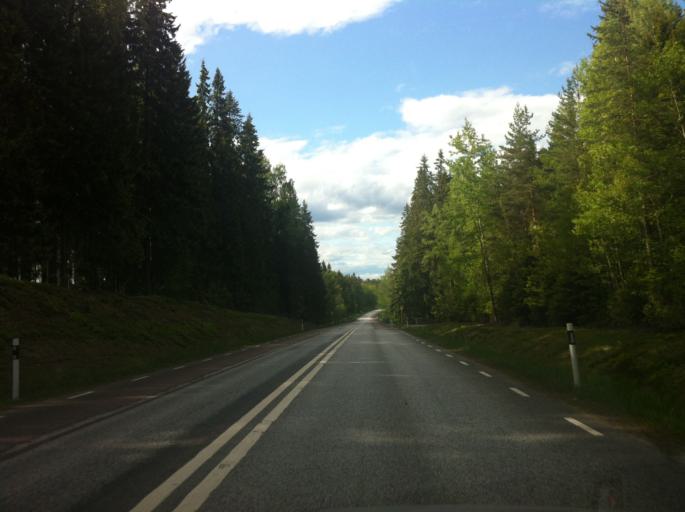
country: SE
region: Vaermland
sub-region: Storfors Kommun
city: Storfors
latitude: 59.4878
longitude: 14.2559
